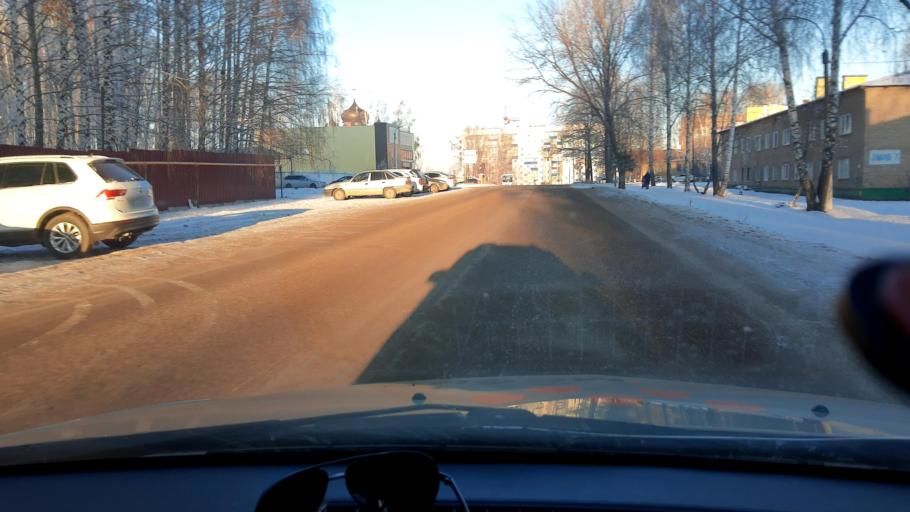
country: RU
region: Bashkortostan
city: Blagoveshchensk
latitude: 55.0494
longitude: 55.9495
